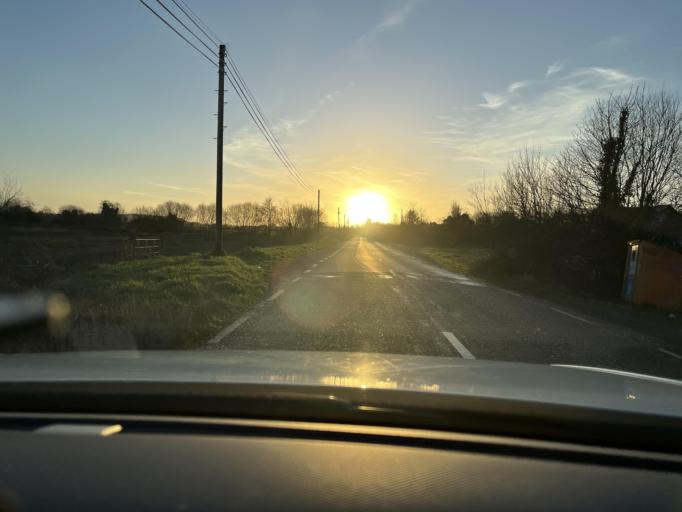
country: IE
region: Ulster
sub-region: An Cabhan
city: Ballyconnell
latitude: 54.1077
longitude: -7.5936
